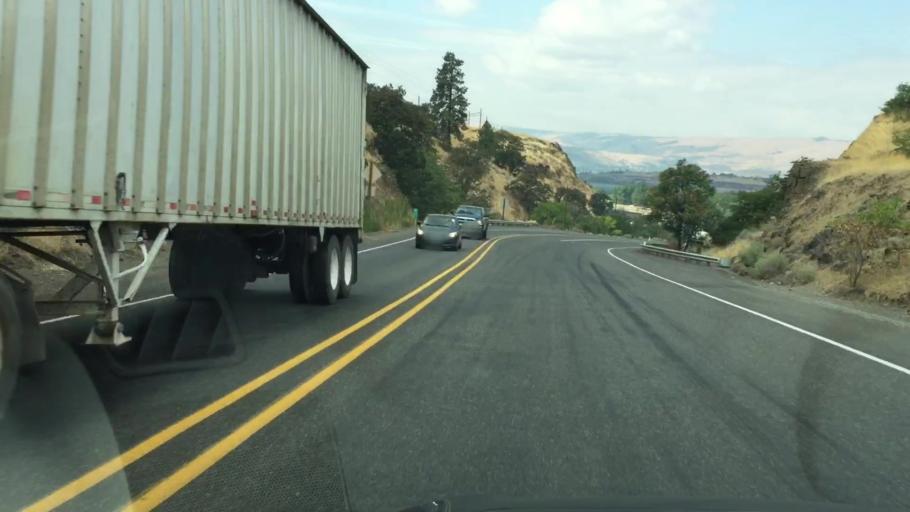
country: US
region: Oregon
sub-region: Wasco County
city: The Dalles
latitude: 45.5978
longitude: -121.1374
